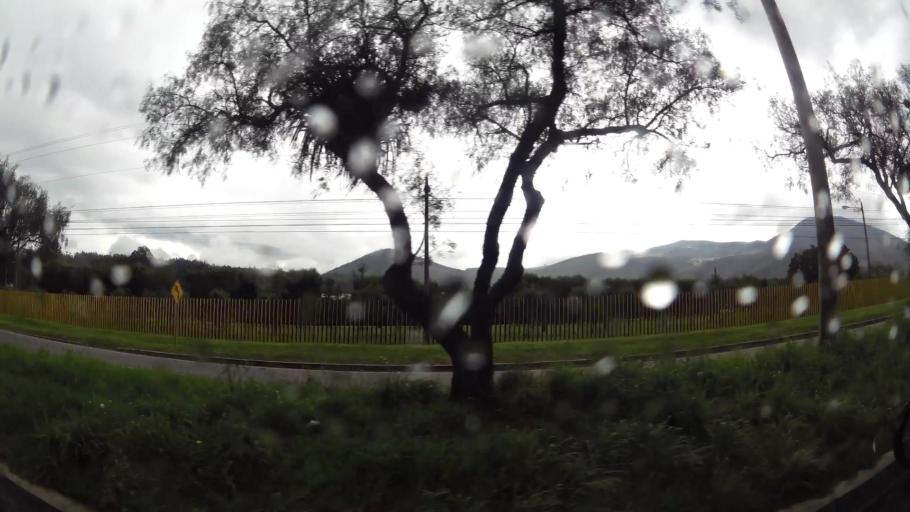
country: EC
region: Pichincha
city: Quito
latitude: -0.0885
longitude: -78.4869
